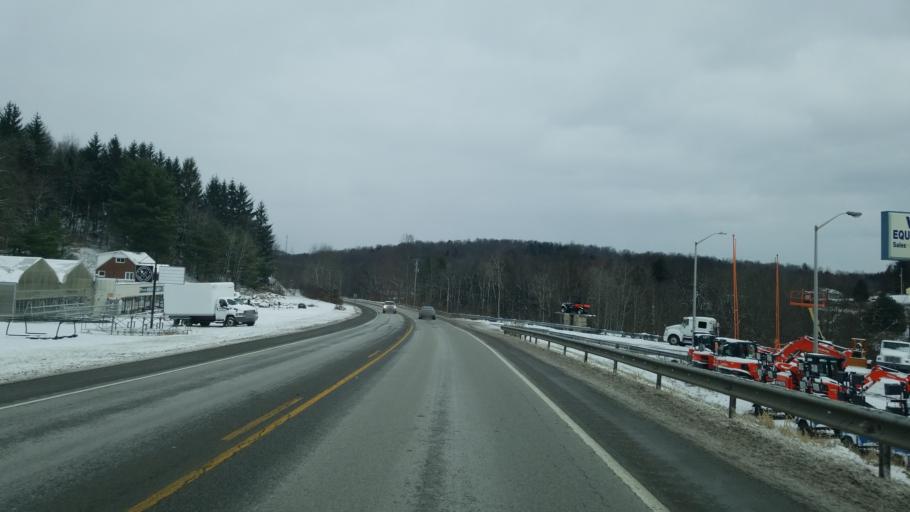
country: US
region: Pennsylvania
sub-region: Clearfield County
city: Sandy
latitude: 41.0874
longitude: -78.7764
